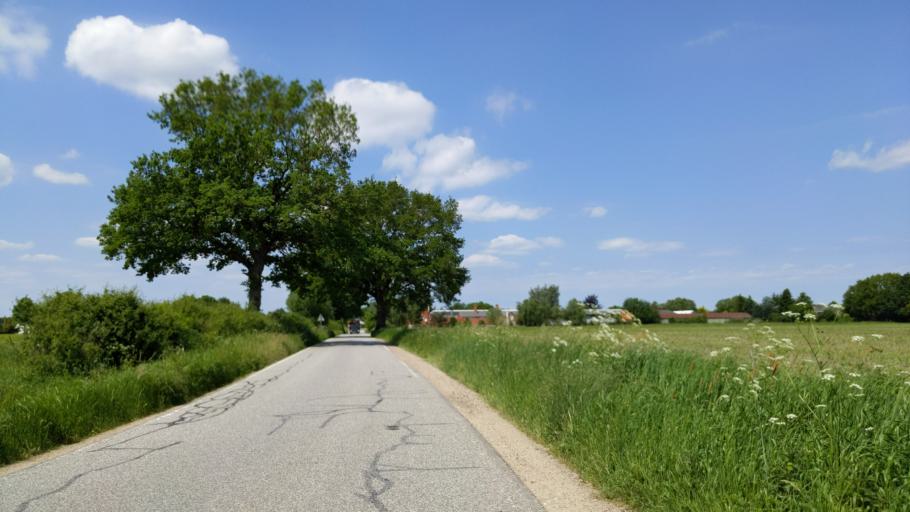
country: DE
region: Schleswig-Holstein
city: Krummesse
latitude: 53.8270
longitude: 10.6621
